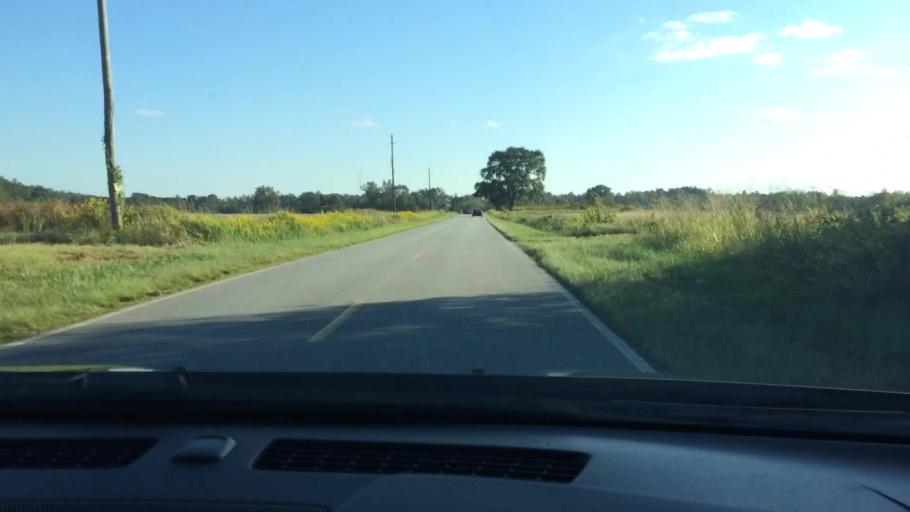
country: US
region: North Carolina
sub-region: Pitt County
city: Winterville
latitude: 35.5086
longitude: -77.4344
